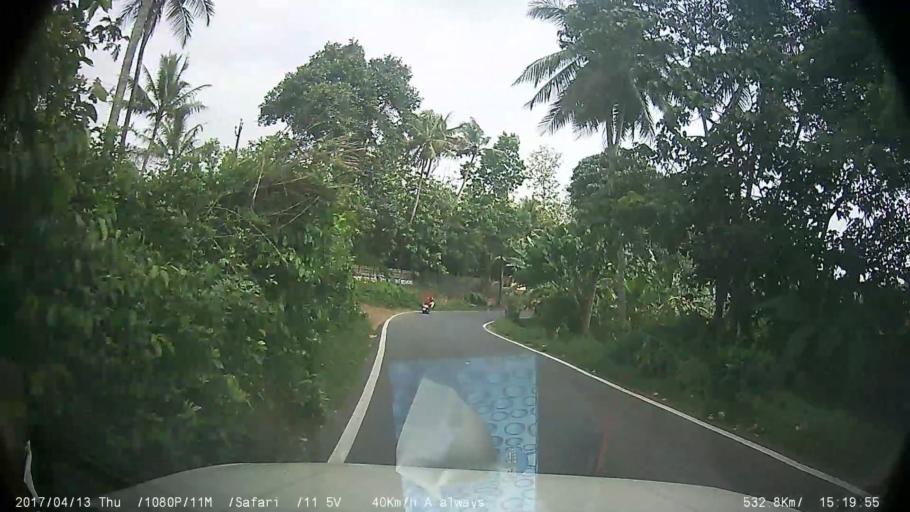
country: IN
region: Kerala
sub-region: Ernakulam
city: Piravam
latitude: 9.8672
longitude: 76.4861
